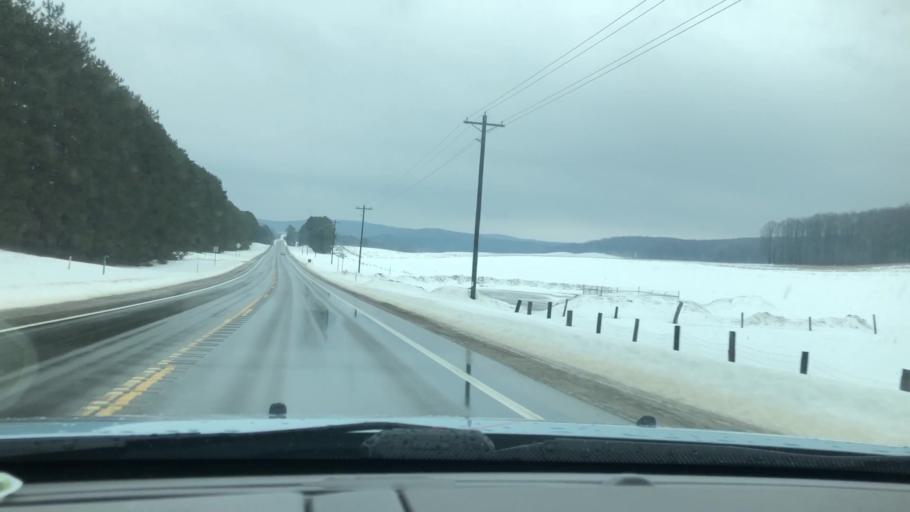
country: US
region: Michigan
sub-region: Charlevoix County
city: Boyne City
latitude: 45.0948
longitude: -84.9745
